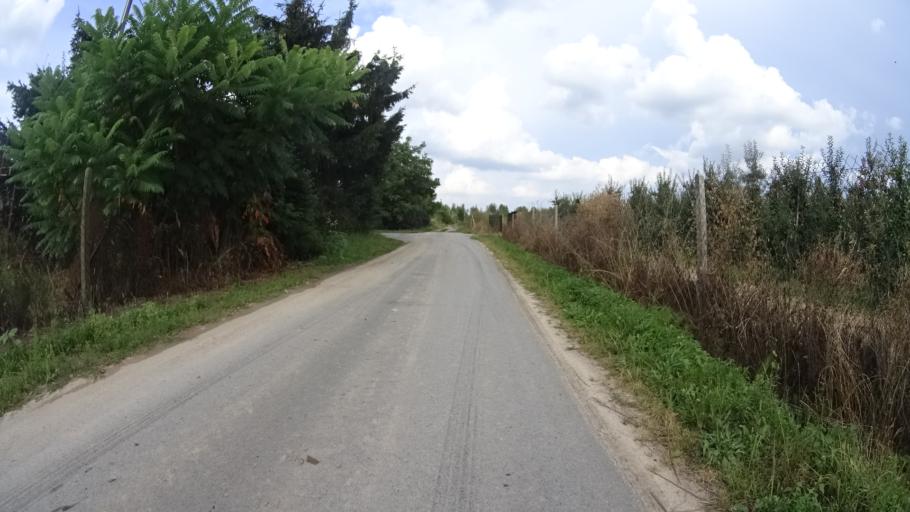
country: PL
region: Masovian Voivodeship
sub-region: Powiat grojecki
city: Goszczyn
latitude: 51.7006
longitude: 20.8200
